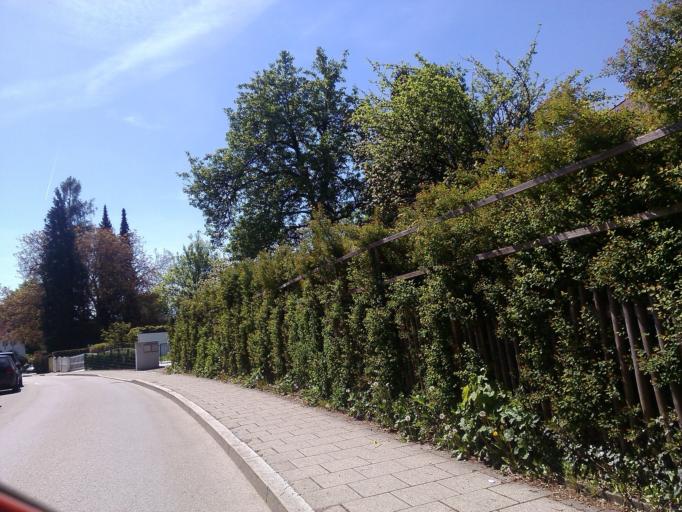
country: DE
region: Bavaria
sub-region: Upper Bavaria
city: Starnberg
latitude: 47.9952
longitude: 11.3381
